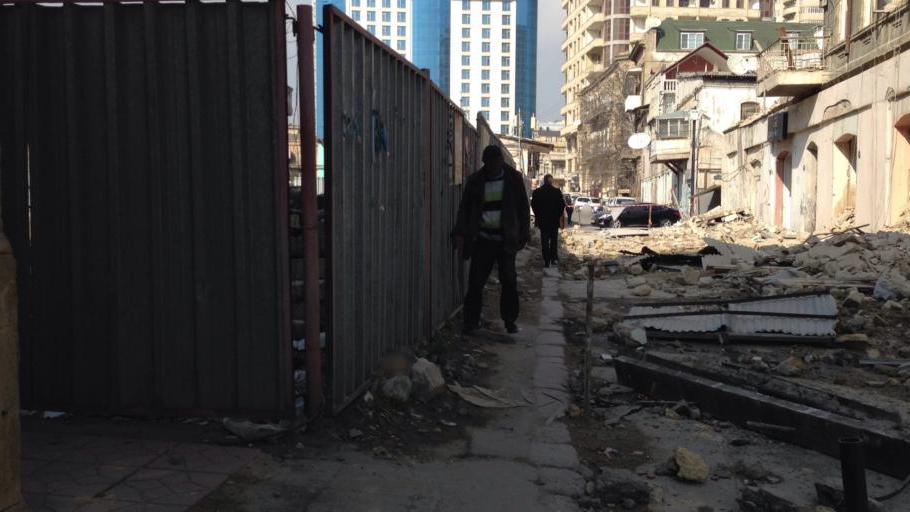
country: AZ
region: Baki
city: Badamdar
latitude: 40.3732
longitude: 49.8384
